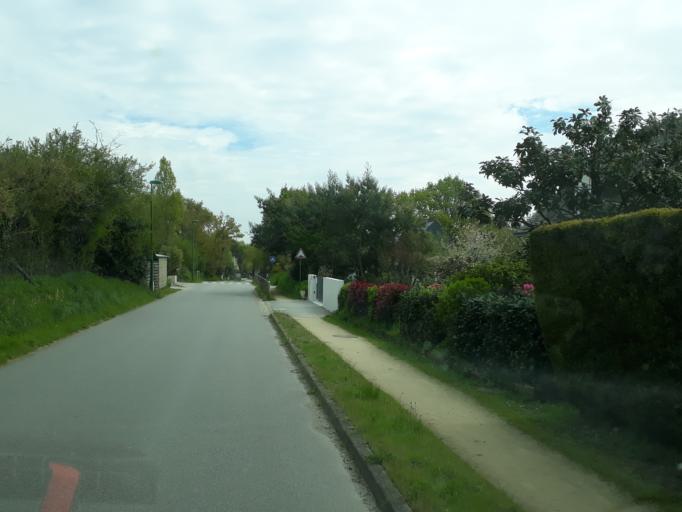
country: FR
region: Brittany
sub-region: Departement du Morbihan
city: Surzur
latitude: 47.5819
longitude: -2.6416
